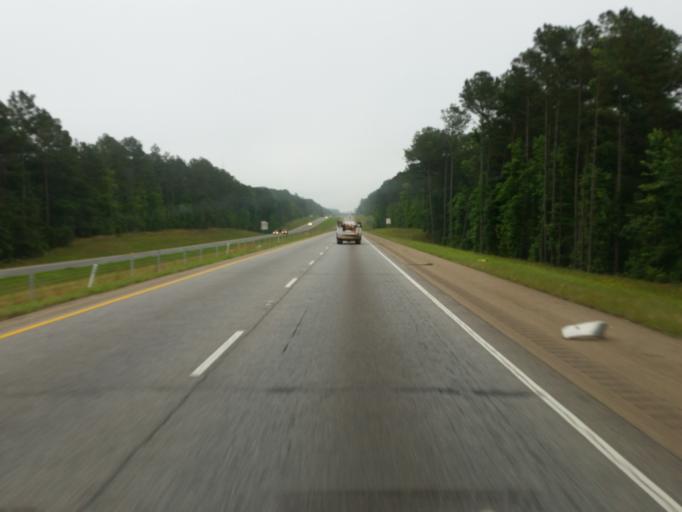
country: US
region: Louisiana
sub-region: Webster Parish
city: Minden
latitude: 32.5789
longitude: -93.2408
